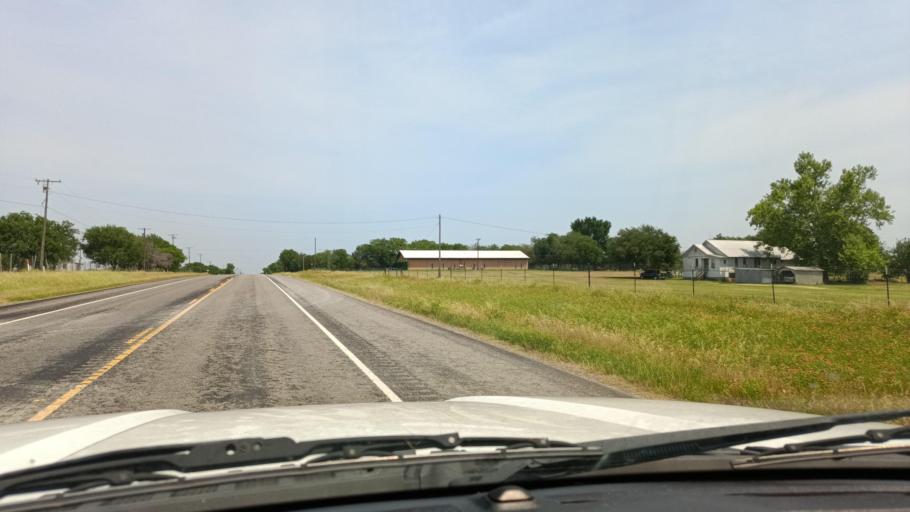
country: US
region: Texas
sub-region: Milam County
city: Cameron
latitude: 30.8527
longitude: -97.0909
